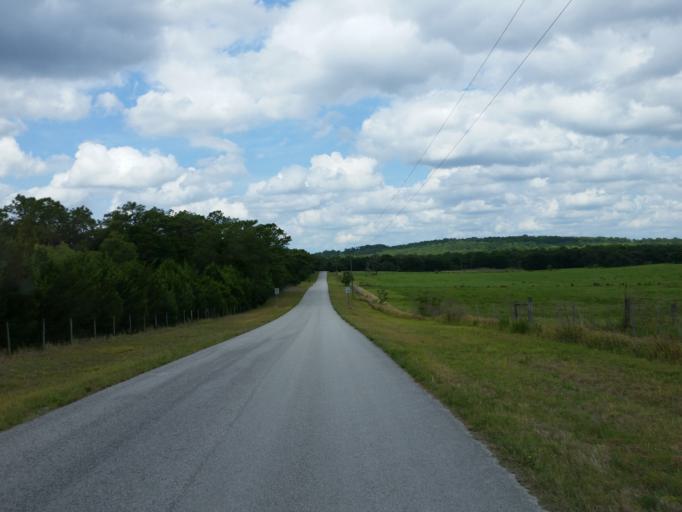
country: US
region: Florida
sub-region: Hernando County
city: Brooksville
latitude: 28.6152
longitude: -82.3436
